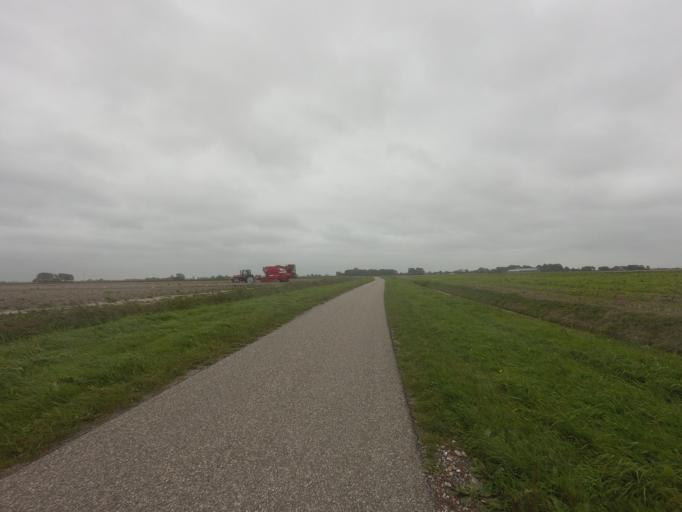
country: NL
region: Friesland
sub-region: Gemeente Ferwerderadiel
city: Ferwert
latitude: 53.3447
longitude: 5.8577
